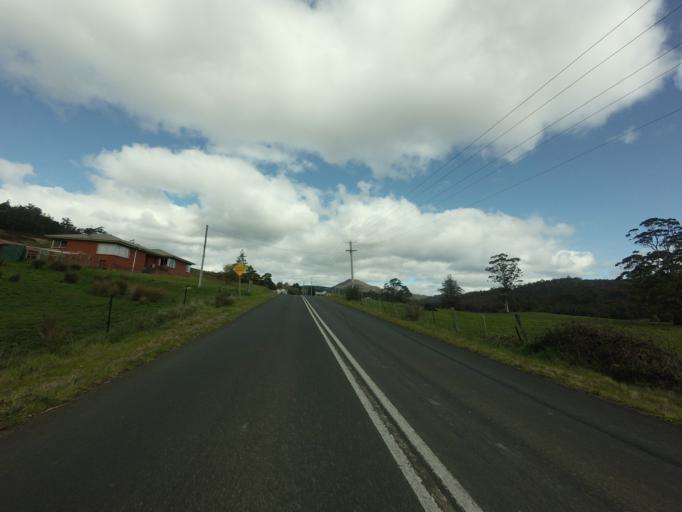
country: AU
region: Tasmania
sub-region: Huon Valley
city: Geeveston
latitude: -43.1824
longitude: 146.9289
